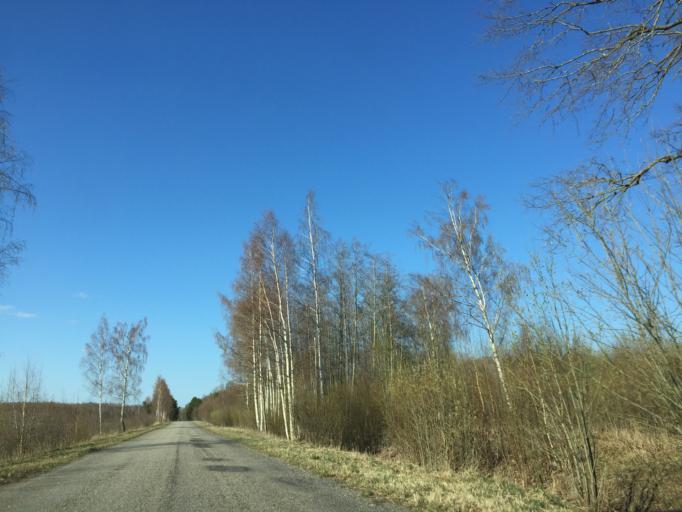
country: EE
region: Valgamaa
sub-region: Torva linn
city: Torva
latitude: 58.2467
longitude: 25.9491
